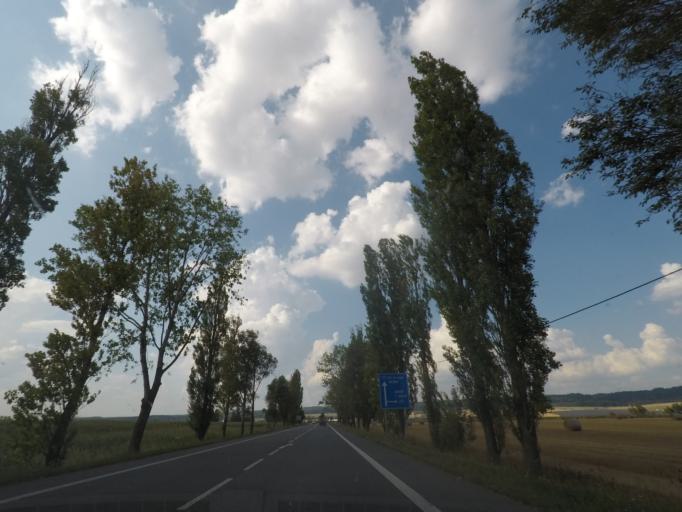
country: CZ
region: Kralovehradecky
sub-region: Okres Nachod
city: Jaromer
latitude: 50.4146
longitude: 15.8844
